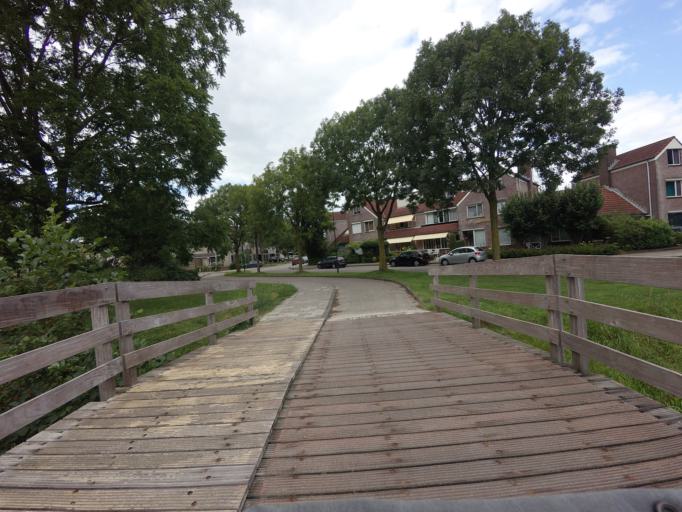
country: NL
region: Utrecht
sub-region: Gemeente IJsselstein
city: IJsselstein
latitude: 52.0232
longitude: 5.0245
